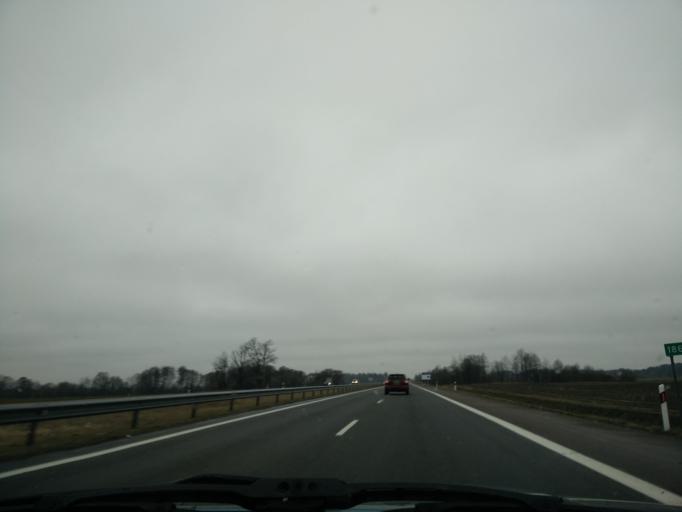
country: LT
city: Raseiniai
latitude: 55.3806
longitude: 22.9227
